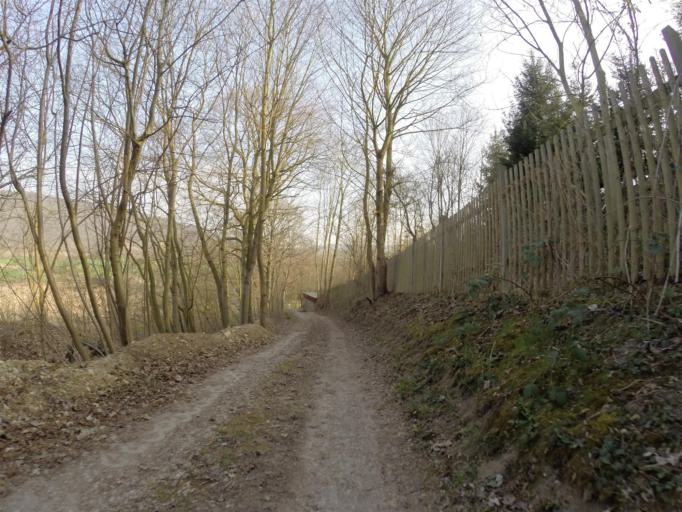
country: DE
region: Thuringia
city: Neuengonna
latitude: 50.9905
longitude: 11.6611
